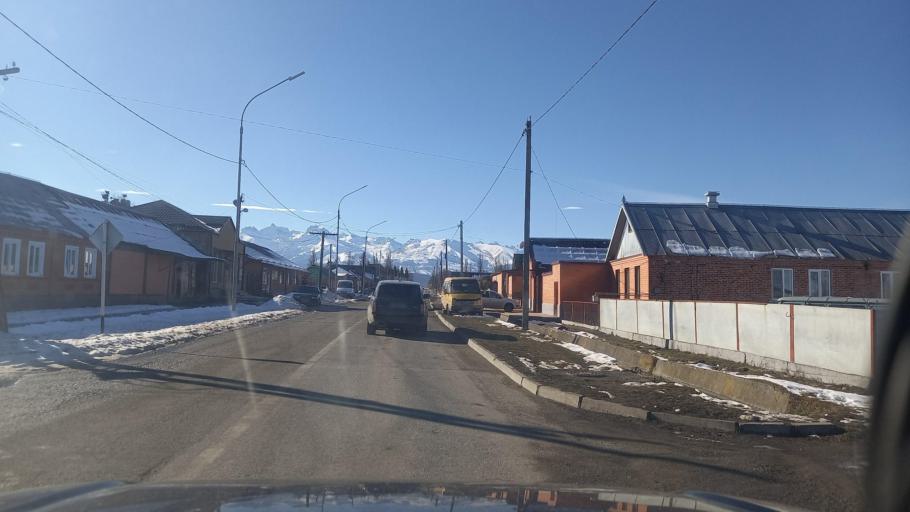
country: RU
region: North Ossetia
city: Chikola
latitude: 43.1885
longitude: 43.9048
